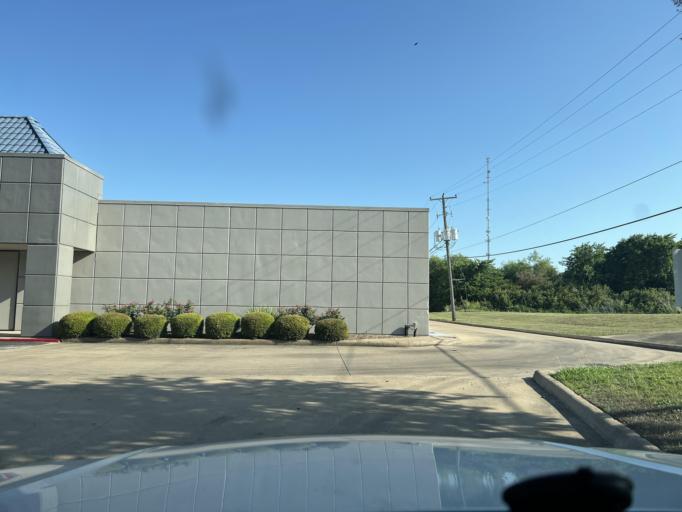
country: US
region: Texas
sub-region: Washington County
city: Brenham
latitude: 30.1415
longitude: -96.3982
